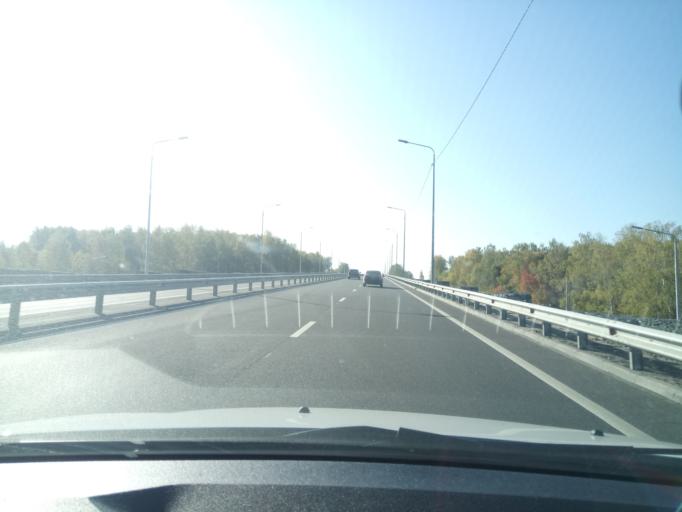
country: RU
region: Nizjnij Novgorod
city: Burevestnik
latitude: 56.0060
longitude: 43.9667
